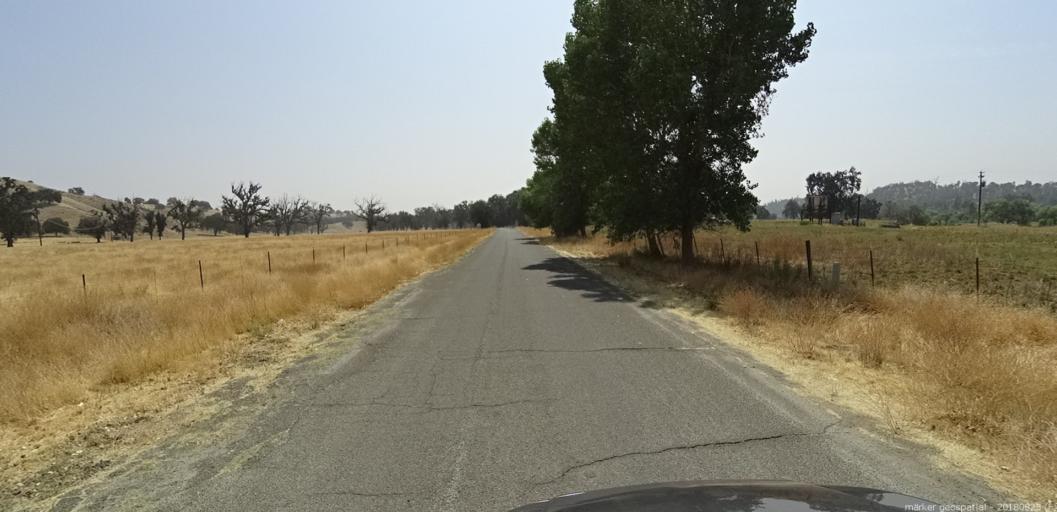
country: US
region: California
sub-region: San Luis Obispo County
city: Shandon
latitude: 35.8861
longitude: -120.4352
